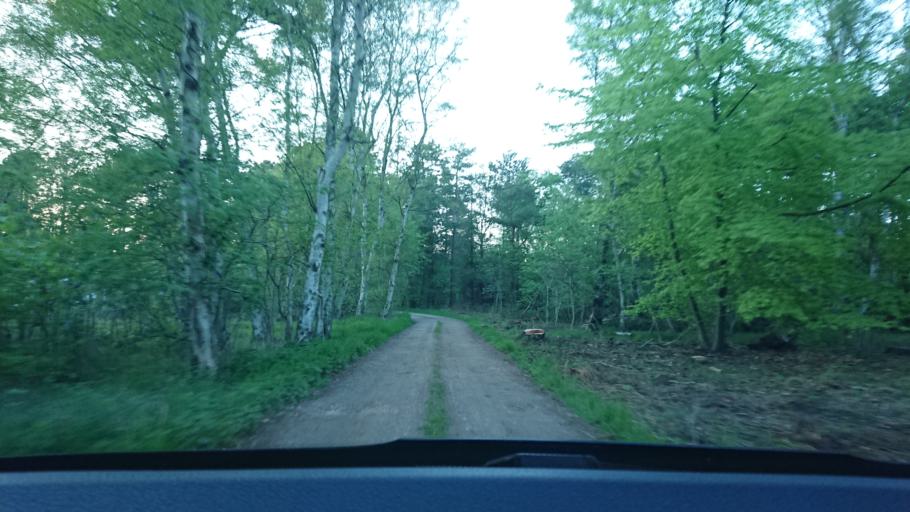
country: DK
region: Zealand
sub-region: Odsherred Kommune
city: Nykobing Sjaelland
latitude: 55.9429
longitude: 11.6962
